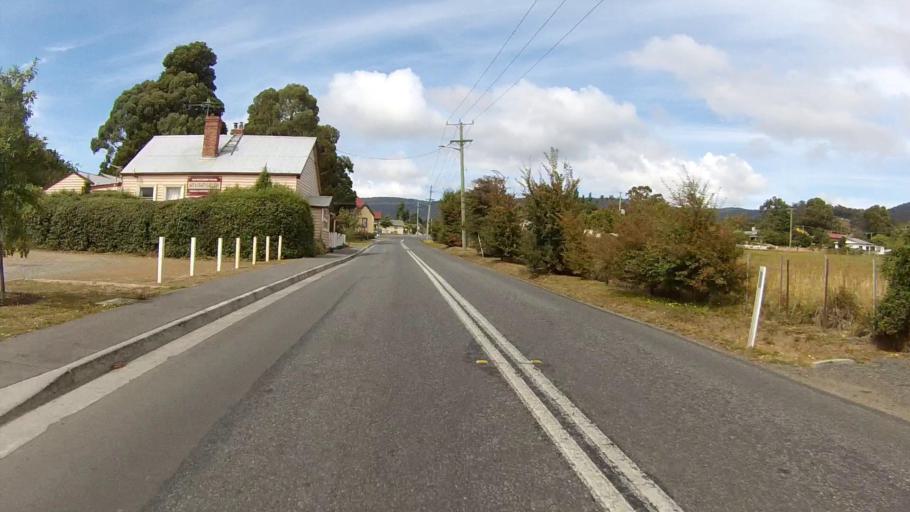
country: AU
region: Tasmania
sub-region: Kingborough
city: Kettering
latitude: -43.1586
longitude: 147.2395
